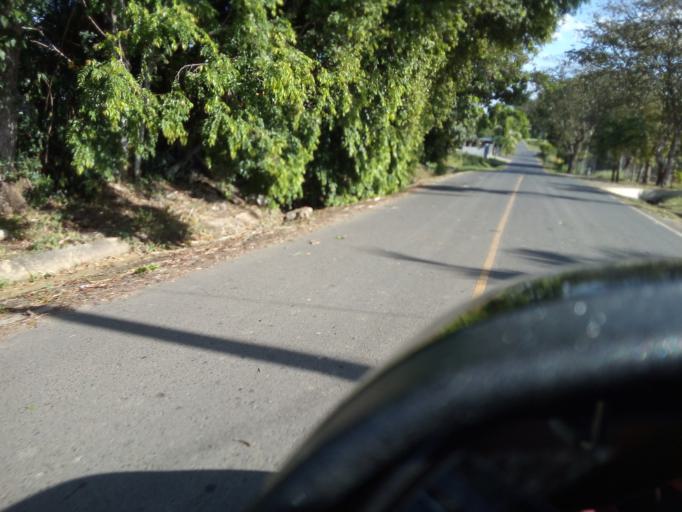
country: PA
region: Veraguas
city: Atalaya
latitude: 8.0417
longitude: -80.9259
